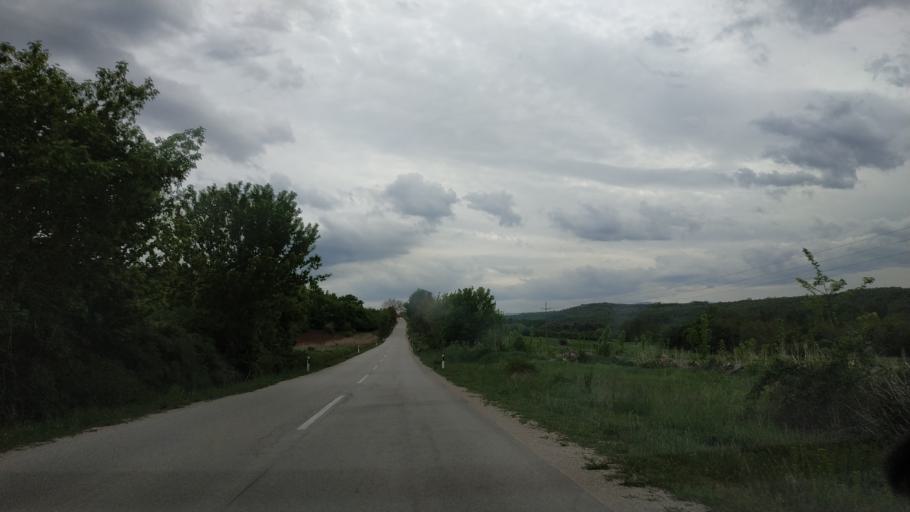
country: RS
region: Central Serbia
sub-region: Nisavski Okrug
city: Aleksinac
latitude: 43.6151
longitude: 21.6902
